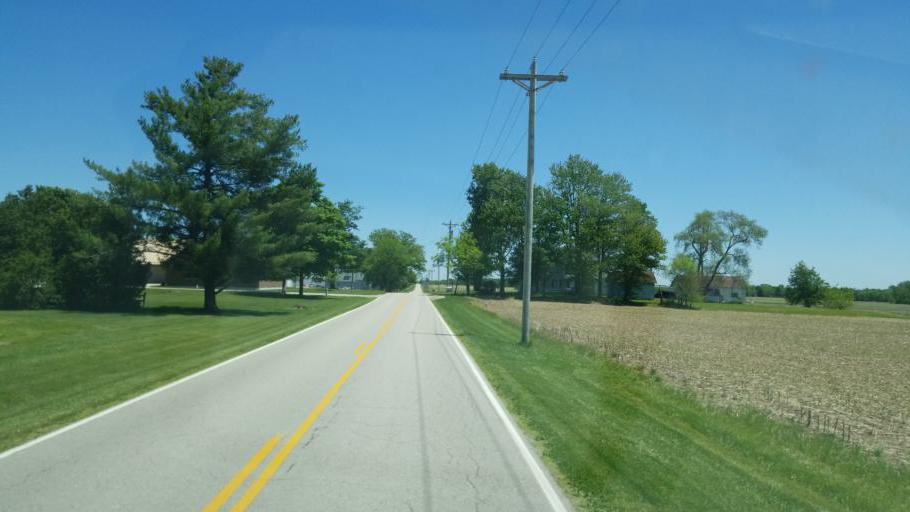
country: US
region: Ohio
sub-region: Darke County
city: Ansonia
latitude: 40.2648
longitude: -84.6715
